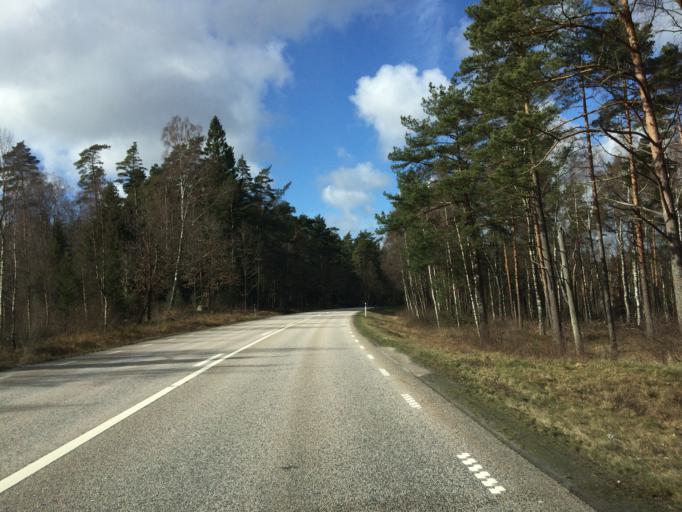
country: SE
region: Halland
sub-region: Laholms Kommun
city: Knared
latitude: 56.4945
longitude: 13.3851
